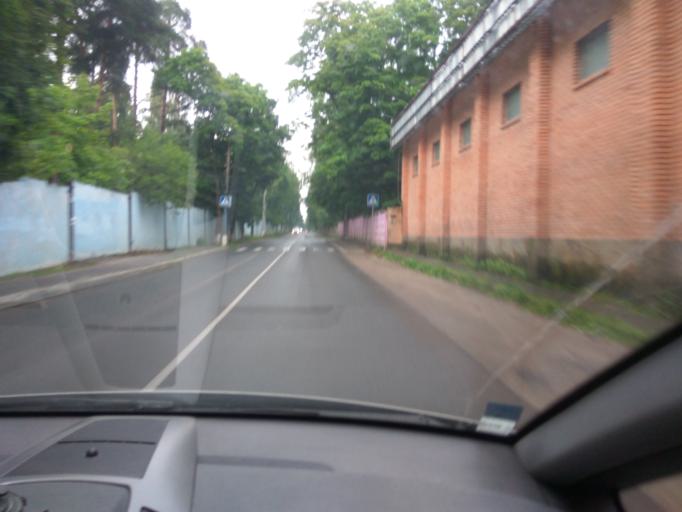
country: RU
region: Moskovskaya
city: Bykovo
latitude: 55.6260
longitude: 38.0847
